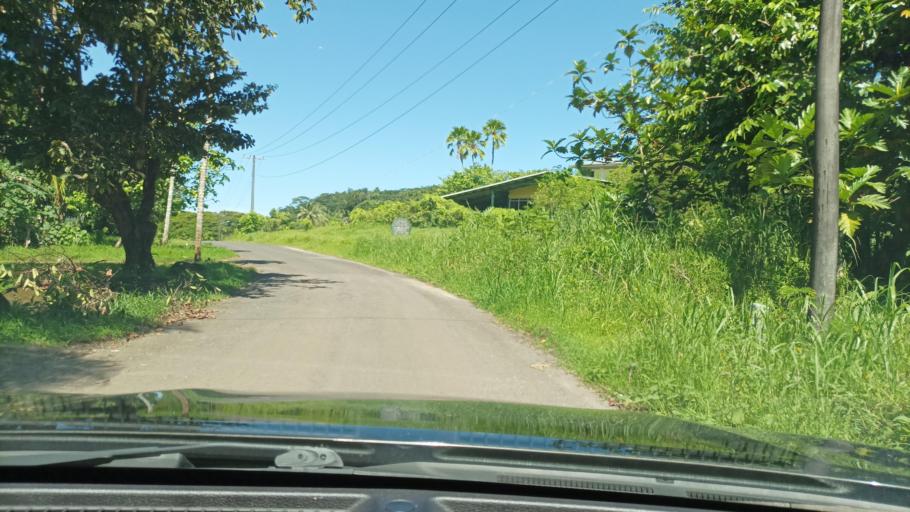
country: FM
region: Pohnpei
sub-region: Madolenihm Municipality
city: Madolenihm Municipality Government
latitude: 6.8427
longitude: 158.3067
